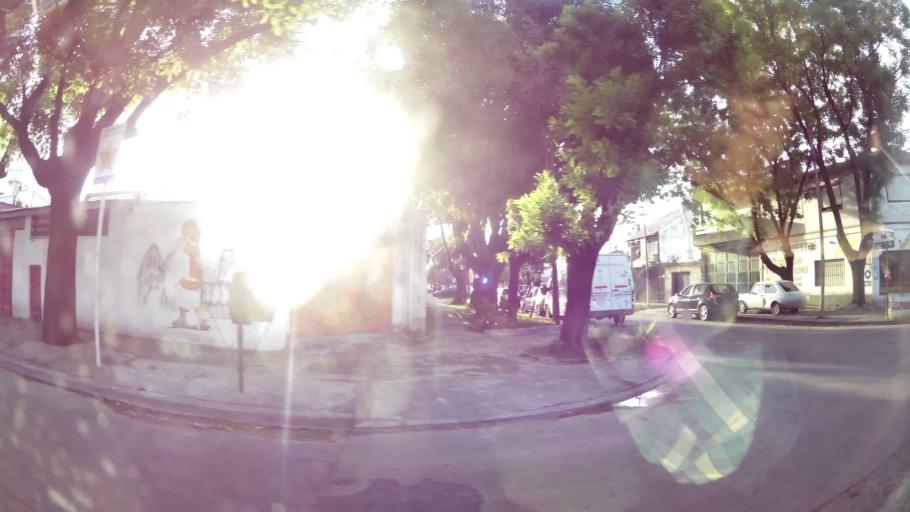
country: AR
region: Buenos Aires
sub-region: Partido de Moron
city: Moron
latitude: -34.6556
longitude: -58.6300
